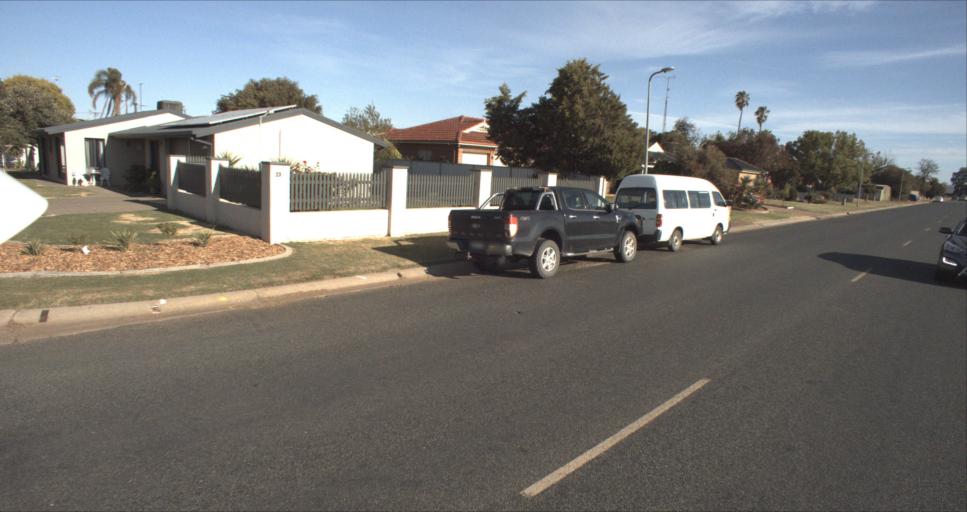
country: AU
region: New South Wales
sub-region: Leeton
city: Leeton
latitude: -34.5433
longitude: 146.3996
